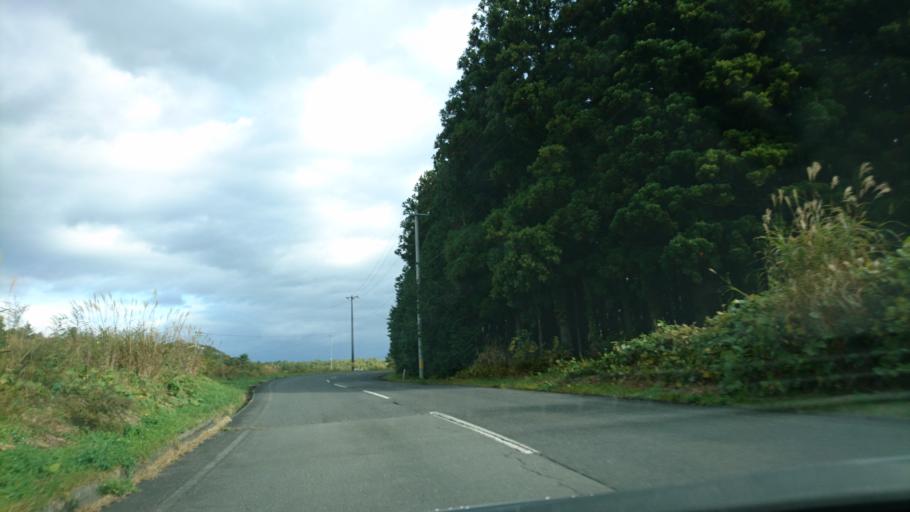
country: JP
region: Iwate
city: Mizusawa
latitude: 39.0971
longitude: 140.9792
